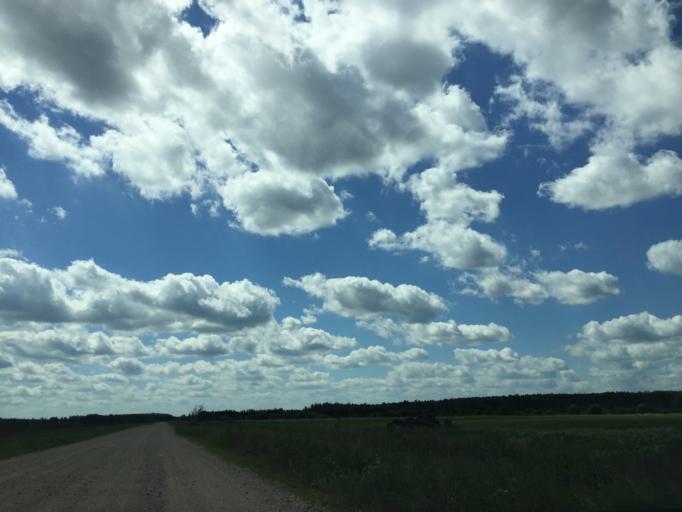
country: LV
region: Olaine
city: Olaine
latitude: 56.8663
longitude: 23.9551
